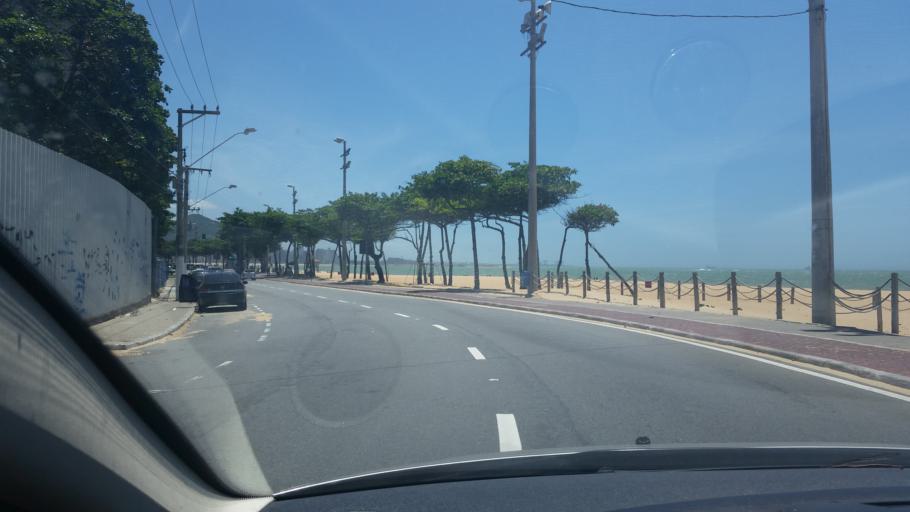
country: BR
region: Espirito Santo
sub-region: Vila Velha
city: Vila Velha
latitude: -20.3536
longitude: -40.2843
